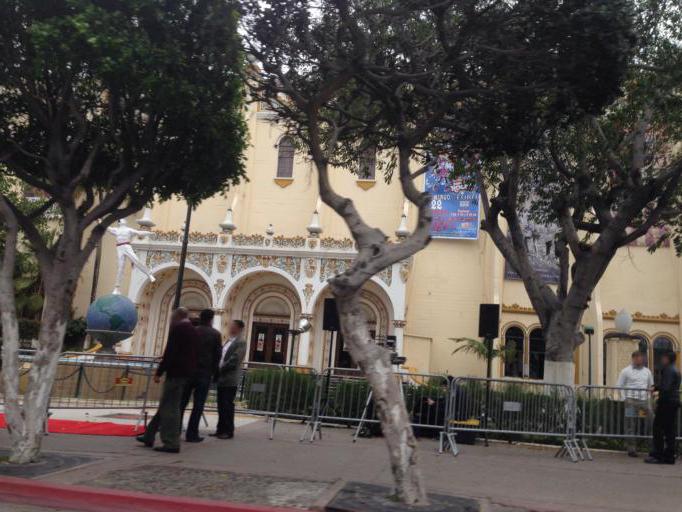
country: MX
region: Baja California
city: Tijuana
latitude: 32.5286
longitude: -117.0362
